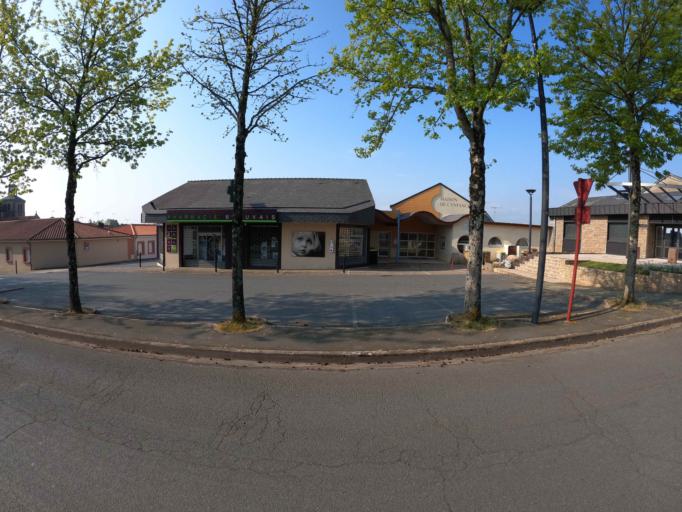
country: FR
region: Pays de la Loire
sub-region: Departement de Maine-et-Loire
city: La Seguiniere
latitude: 47.0629
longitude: -0.9410
